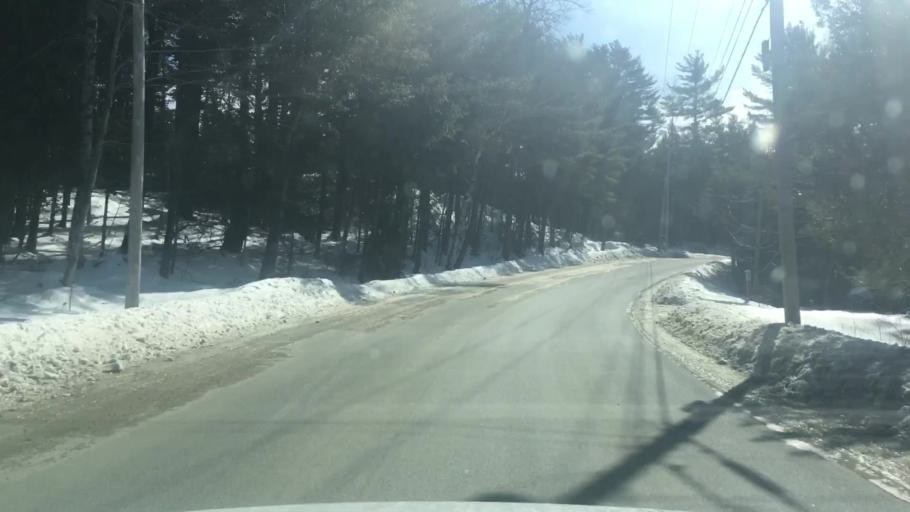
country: US
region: Maine
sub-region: Penobscot County
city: Holden
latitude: 44.7506
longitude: -68.6326
